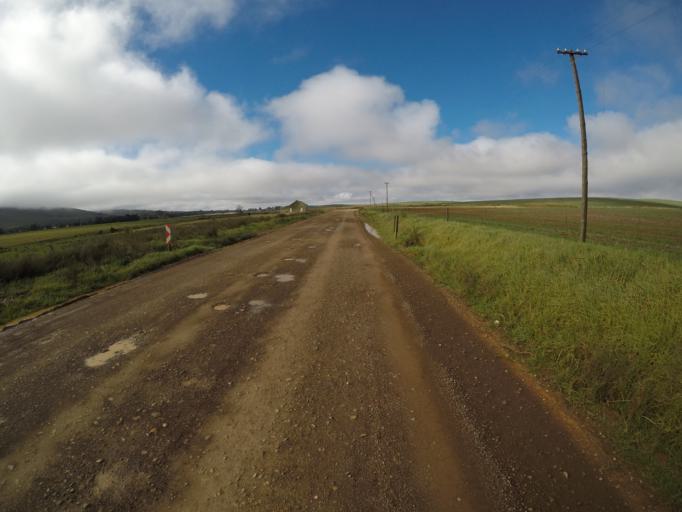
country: ZA
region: Western Cape
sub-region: Cape Winelands District Municipality
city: Ashton
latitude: -34.1495
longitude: 19.8765
